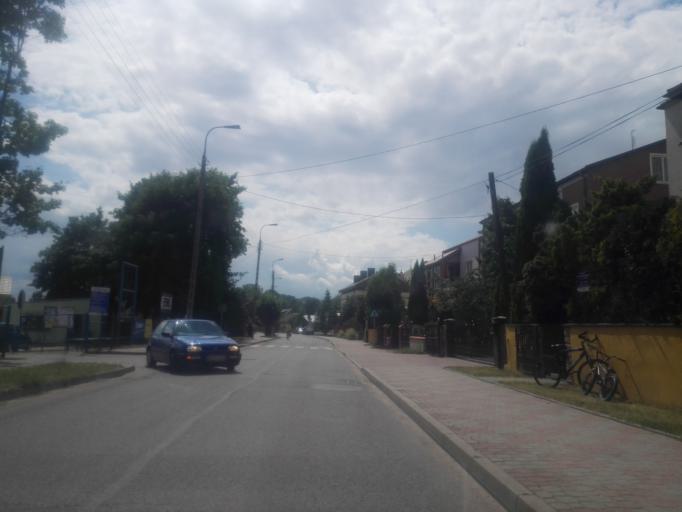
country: PL
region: Podlasie
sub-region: Powiat sejnenski
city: Sejny
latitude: 54.1114
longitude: 23.3503
